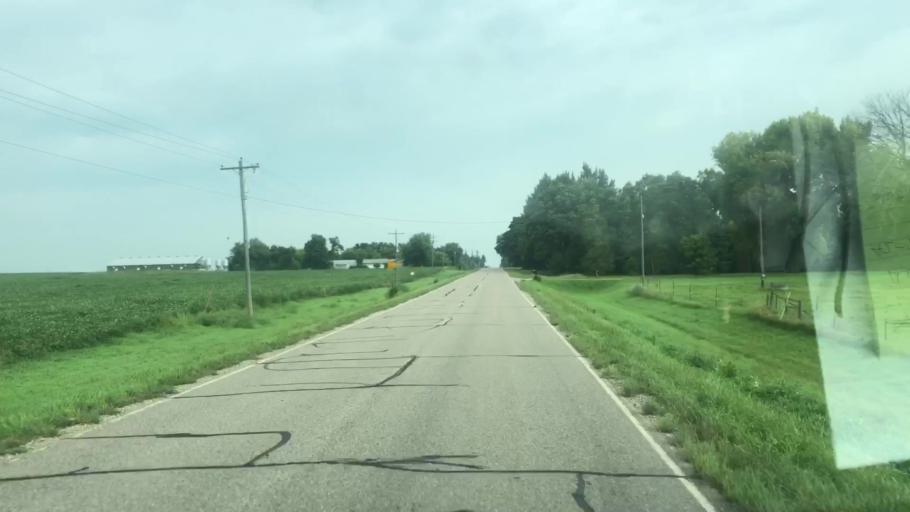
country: US
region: Iowa
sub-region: O'Brien County
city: Sheldon
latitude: 43.2006
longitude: -95.8622
